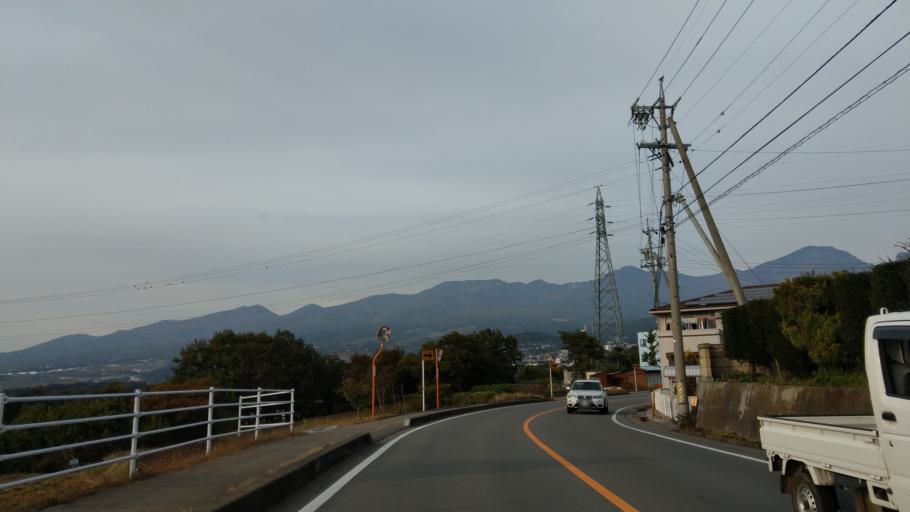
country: JP
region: Nagano
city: Komoro
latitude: 36.3138
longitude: 138.4268
